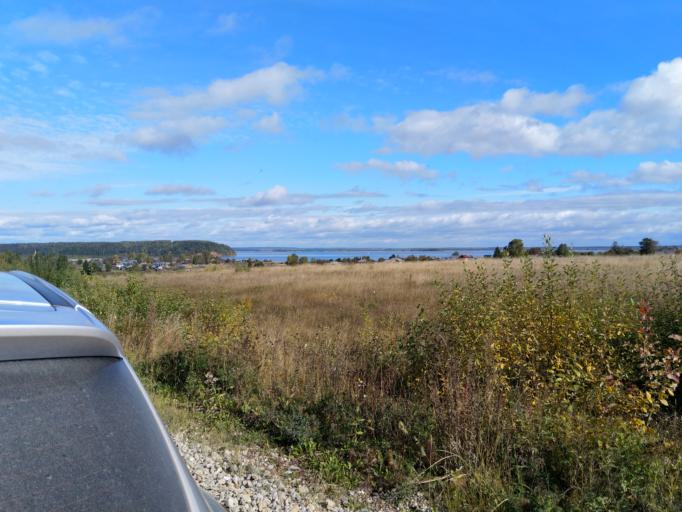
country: RU
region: Perm
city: Pozhva
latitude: 59.1415
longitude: 56.1852
